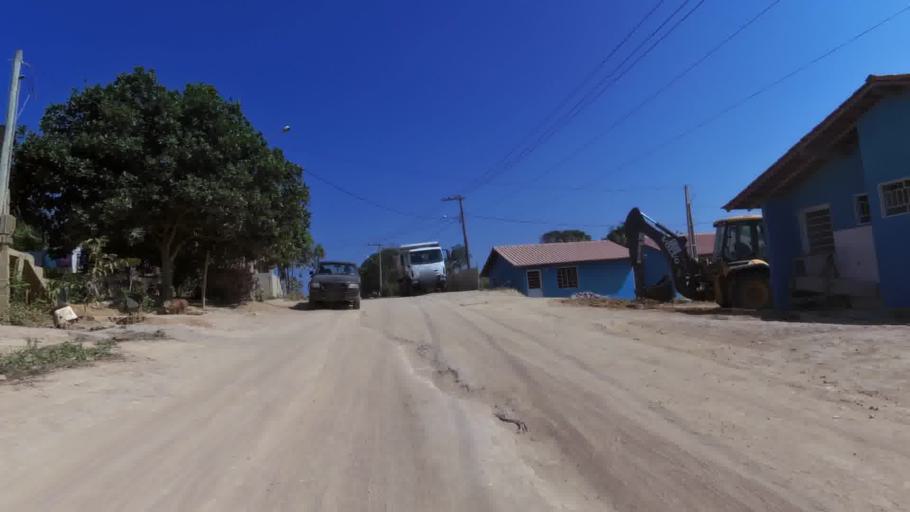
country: BR
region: Espirito Santo
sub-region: Marataizes
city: Marataizes
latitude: -21.0318
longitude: -40.8229
